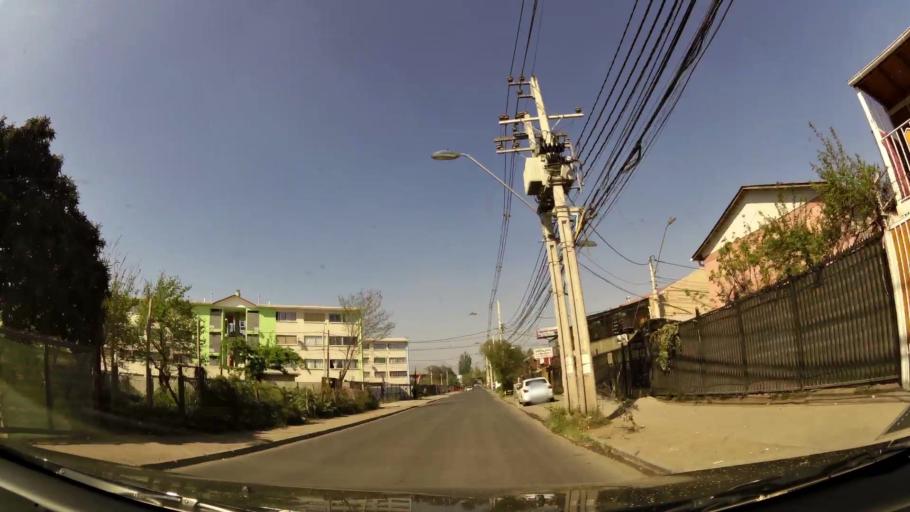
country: CL
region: Santiago Metropolitan
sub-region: Provincia de Santiago
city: Lo Prado
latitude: -33.3553
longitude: -70.7423
